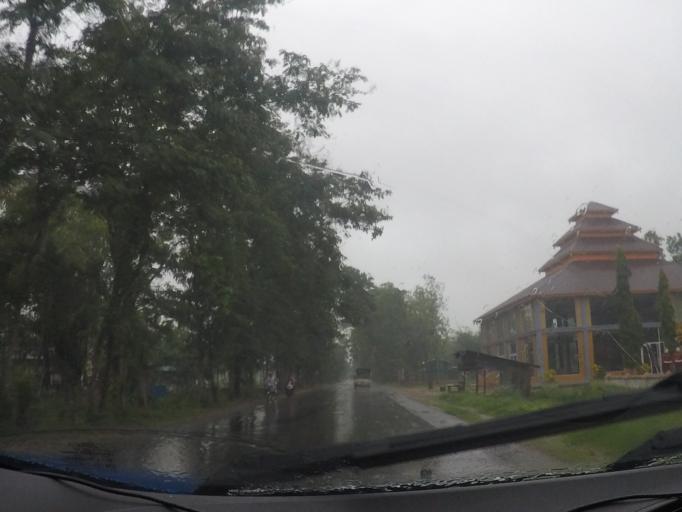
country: MM
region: Bago
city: Letpandan
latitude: 18.1232
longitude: 95.6991
